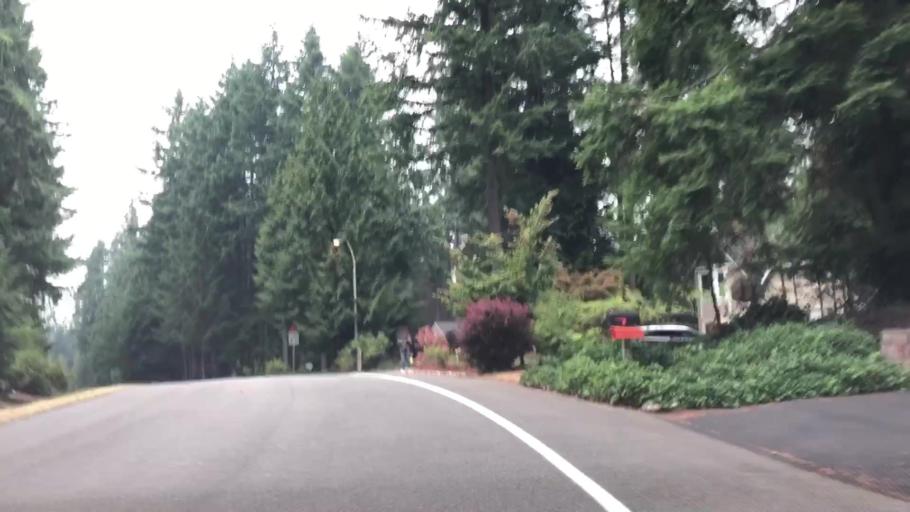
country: US
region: Washington
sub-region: King County
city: Cottage Lake
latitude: 47.7705
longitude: -122.0780
